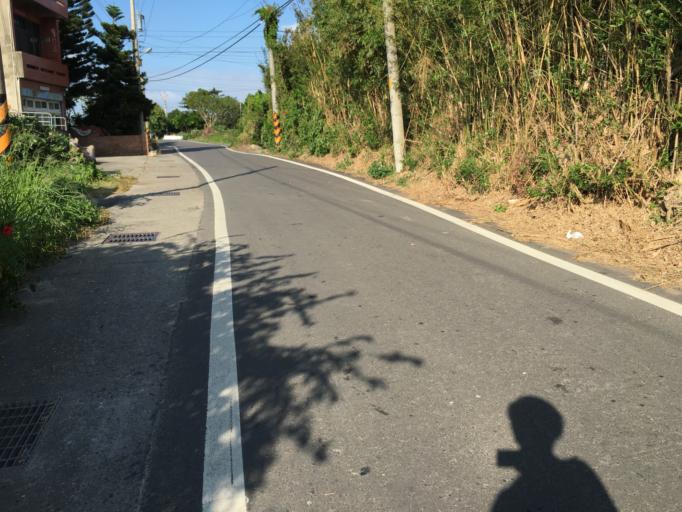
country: TW
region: Taiwan
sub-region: Hsinchu
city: Zhubei
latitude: 24.9255
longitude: 120.9841
